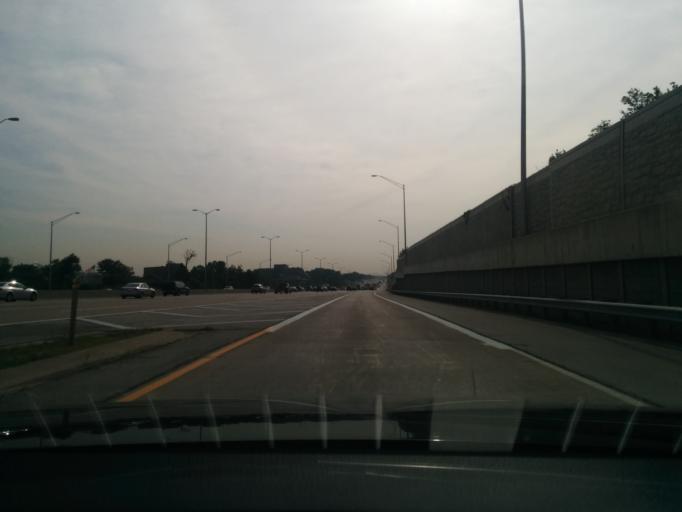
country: US
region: Illinois
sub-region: DuPage County
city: Naperville
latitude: 41.8058
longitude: -88.1171
